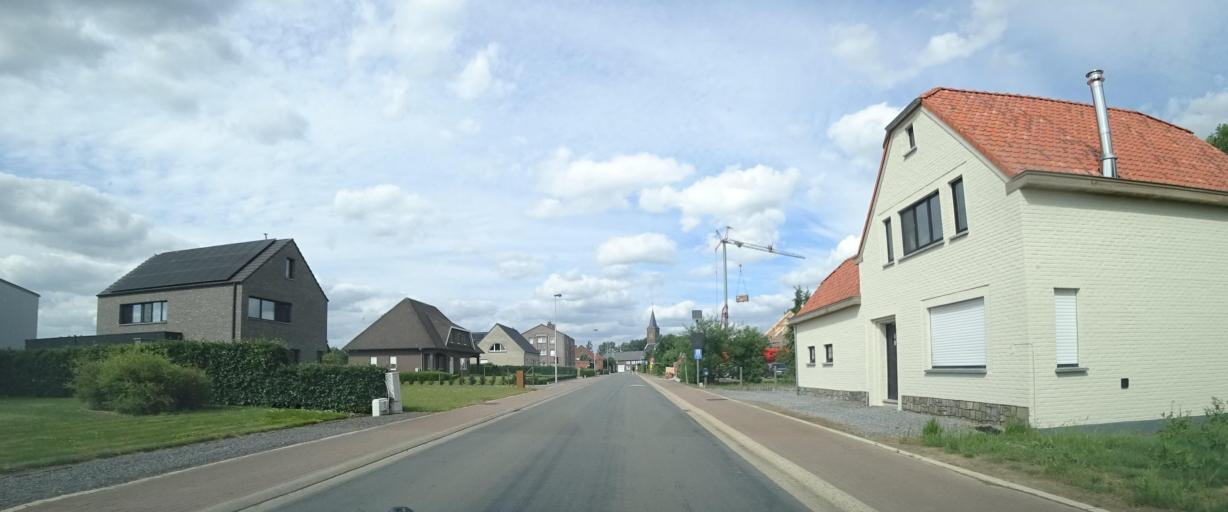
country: BE
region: Flanders
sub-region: Provincie Limburg
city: Nieuwerkerken
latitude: 50.8590
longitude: 5.1632
